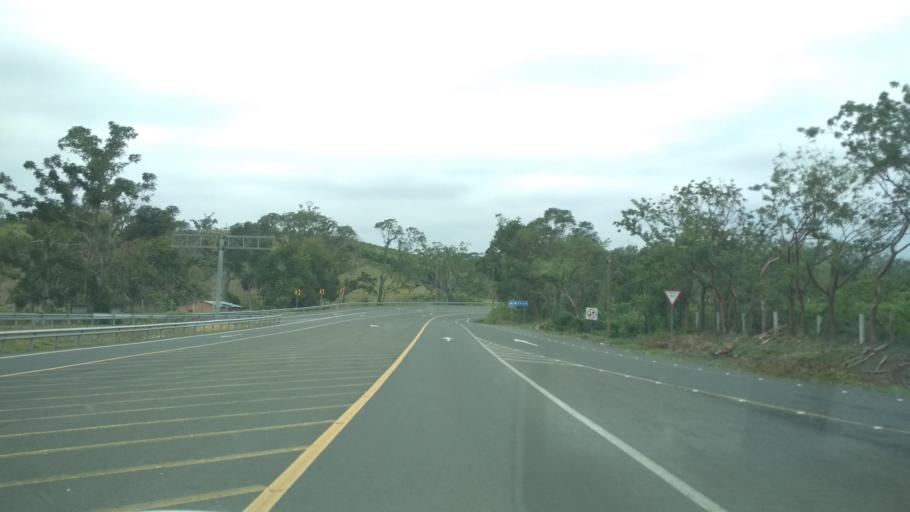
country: MX
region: Veracruz
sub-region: Papantla
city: Polutla
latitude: 20.4599
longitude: -97.2484
